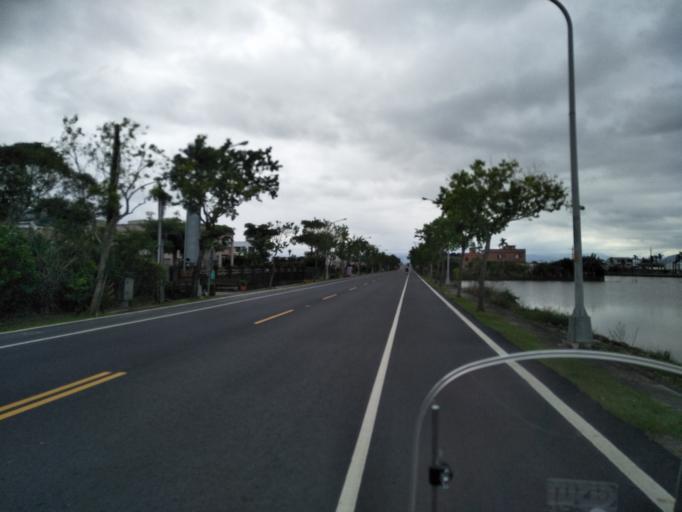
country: TW
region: Taiwan
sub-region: Yilan
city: Yilan
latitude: 24.8142
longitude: 121.7940
